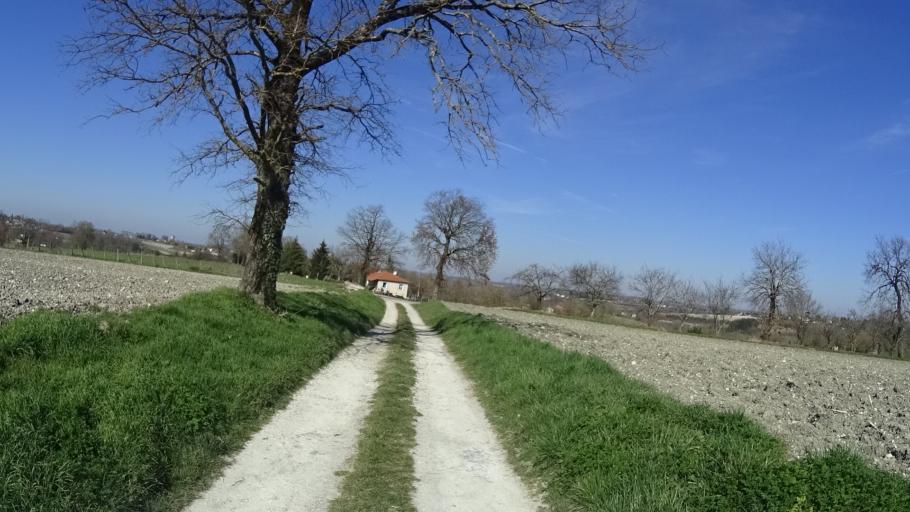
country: FR
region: Aquitaine
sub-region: Departement de la Dordogne
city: Riberac
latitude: 45.2307
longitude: 0.3435
